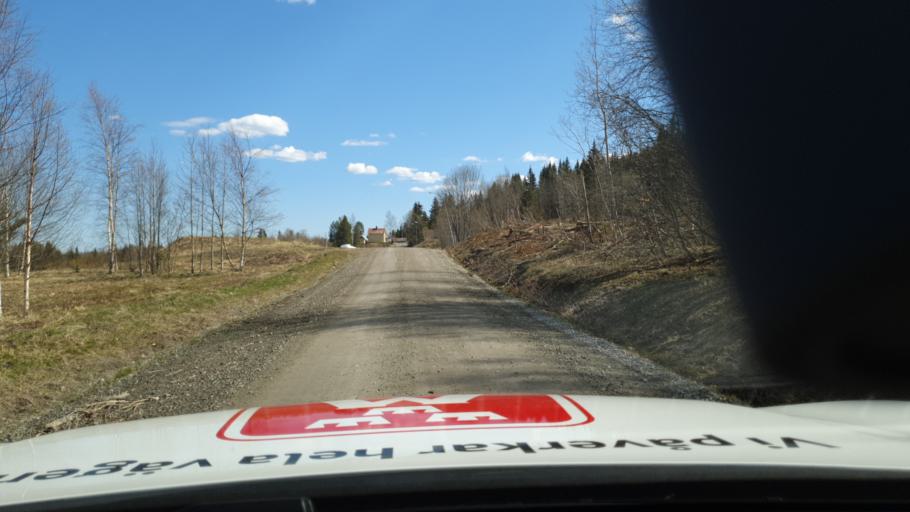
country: SE
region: Jaemtland
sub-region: Bergs Kommun
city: Hoverberg
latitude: 62.9353
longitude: 14.2810
